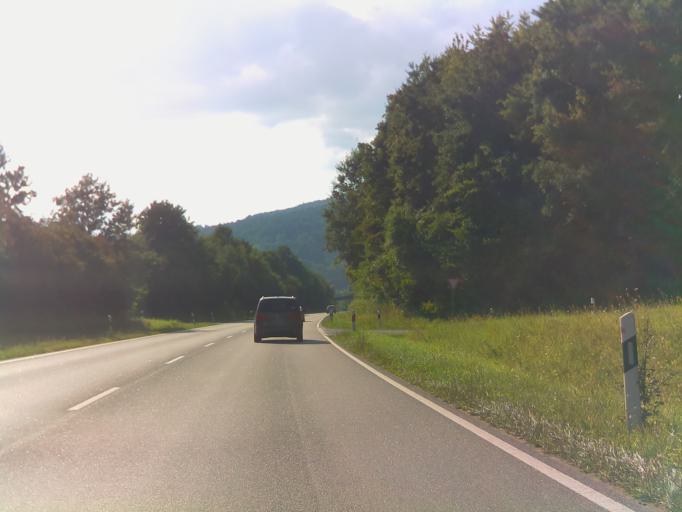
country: DE
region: Bavaria
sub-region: Regierungsbezirk Unterfranken
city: Gemunden
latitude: 50.0641
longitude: 9.6720
